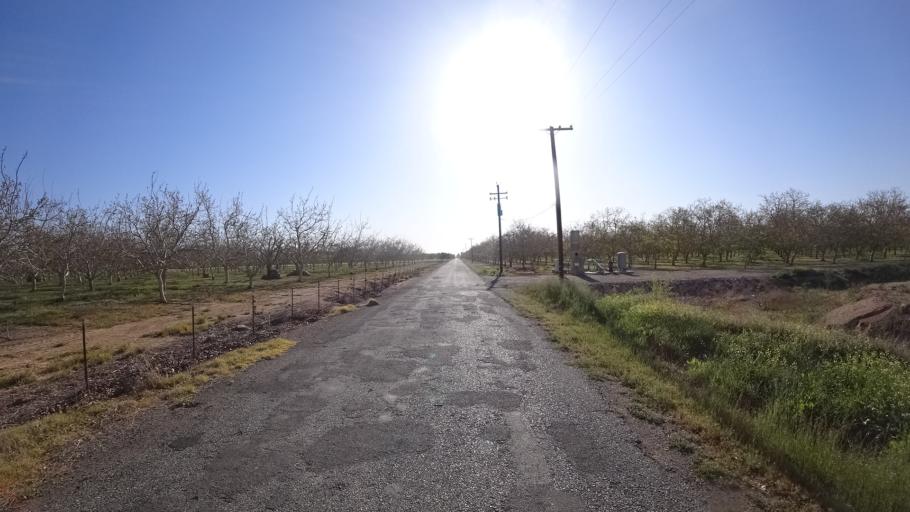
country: US
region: California
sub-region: Glenn County
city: Orland
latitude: 39.6821
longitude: -122.1708
